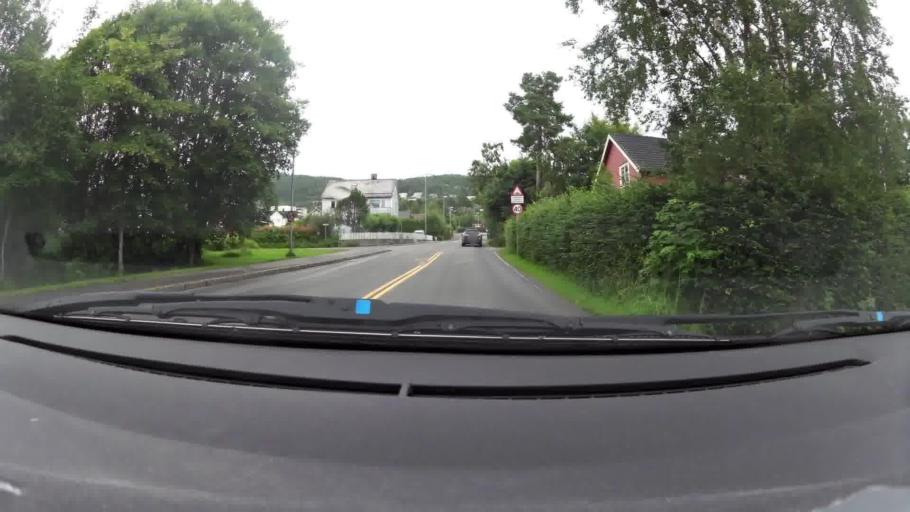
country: NO
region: More og Romsdal
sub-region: Molde
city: Molde
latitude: 62.7429
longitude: 7.2311
